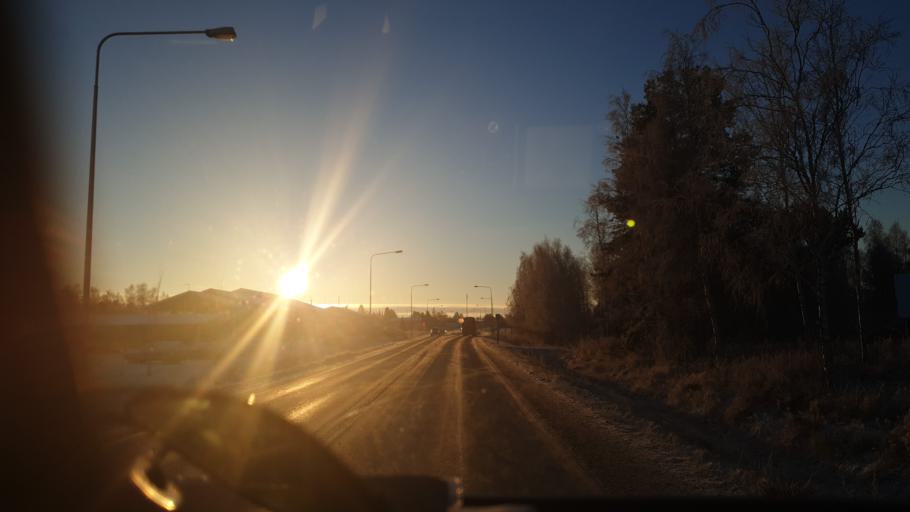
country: FI
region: Northern Ostrobothnia
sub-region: Ylivieska
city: Kalajoki
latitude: 64.2676
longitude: 23.9492
